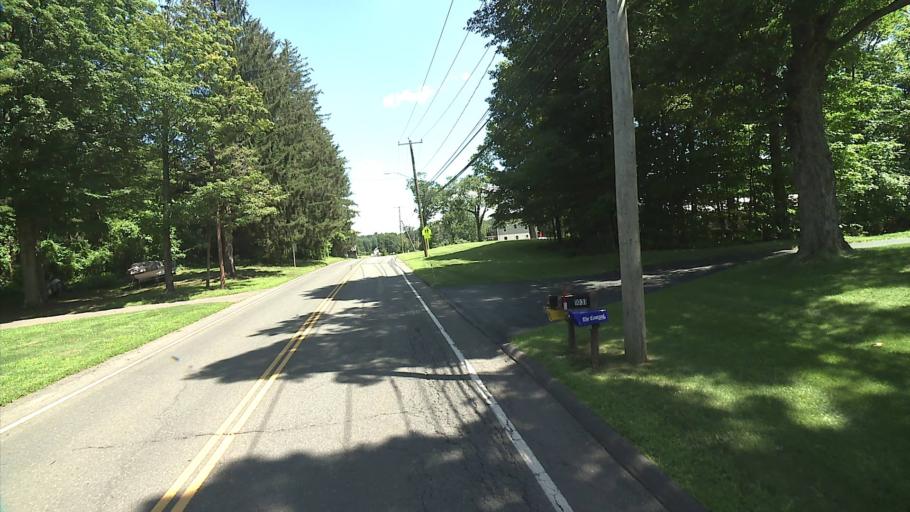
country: US
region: Connecticut
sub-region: Hartford County
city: Suffield Depot
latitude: 41.9867
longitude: -72.6896
